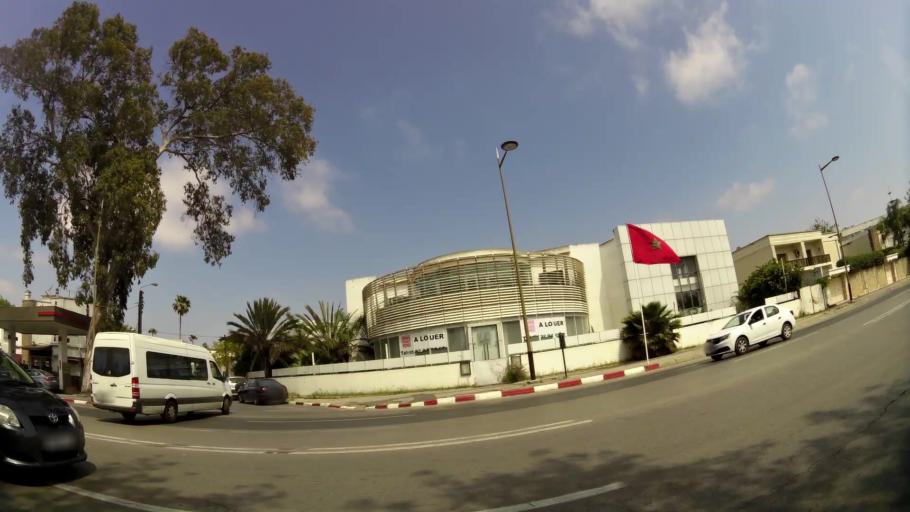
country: MA
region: Rabat-Sale-Zemmour-Zaer
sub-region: Rabat
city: Rabat
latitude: 33.9834
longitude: -6.8292
